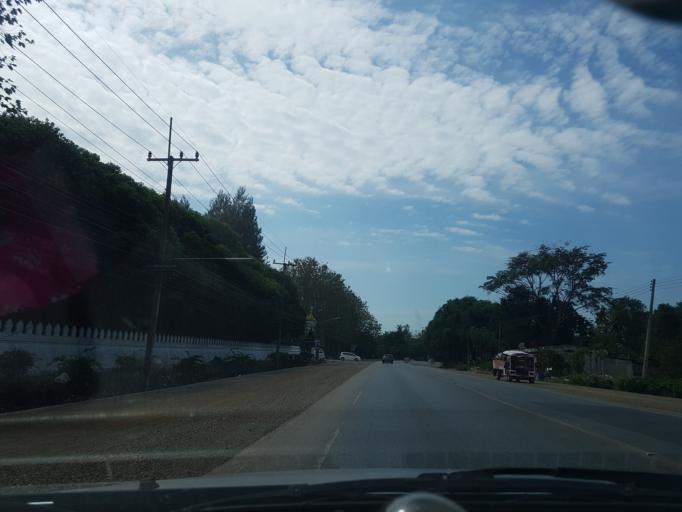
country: TH
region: Sara Buri
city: Phra Phutthabat
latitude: 14.8036
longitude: 100.7590
